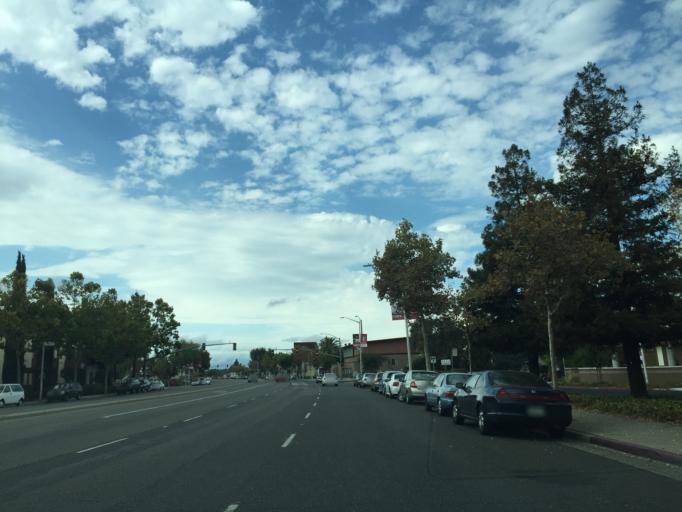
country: US
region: California
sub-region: Santa Clara County
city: Palo Alto
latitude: 37.4150
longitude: -122.1270
